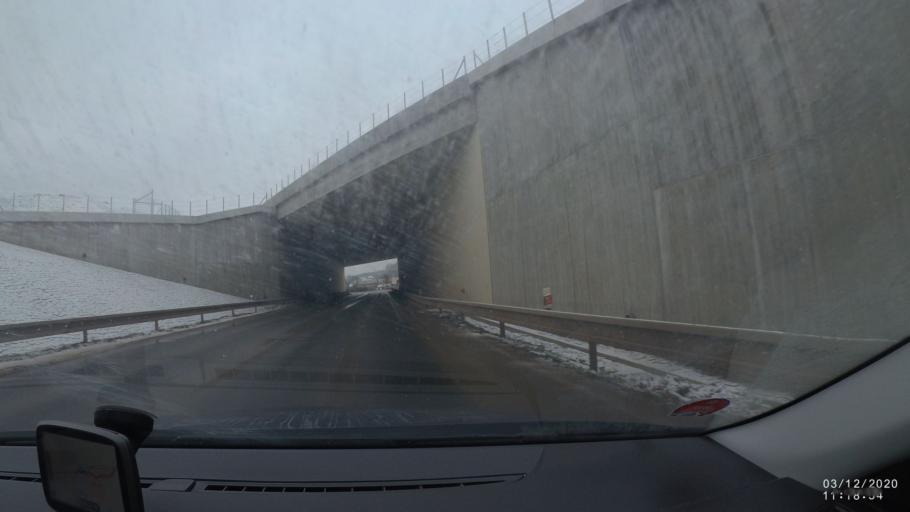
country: CZ
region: Central Bohemia
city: Revnicov
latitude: 50.1757
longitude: 13.7661
